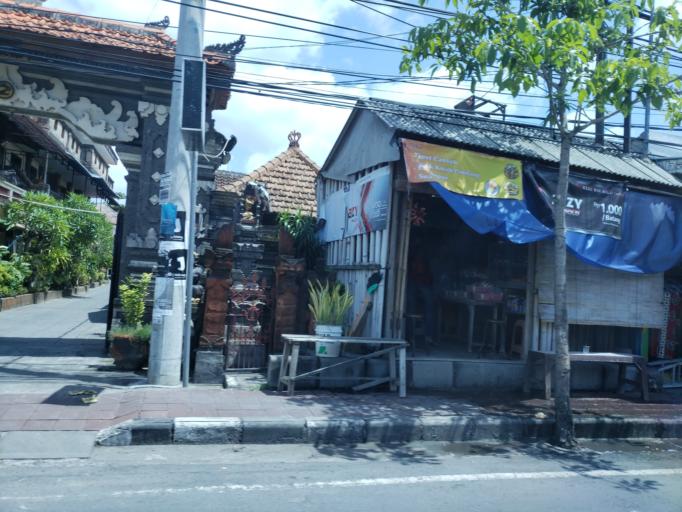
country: ID
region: Bali
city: Jimbaran
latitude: -8.7742
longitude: 115.1720
